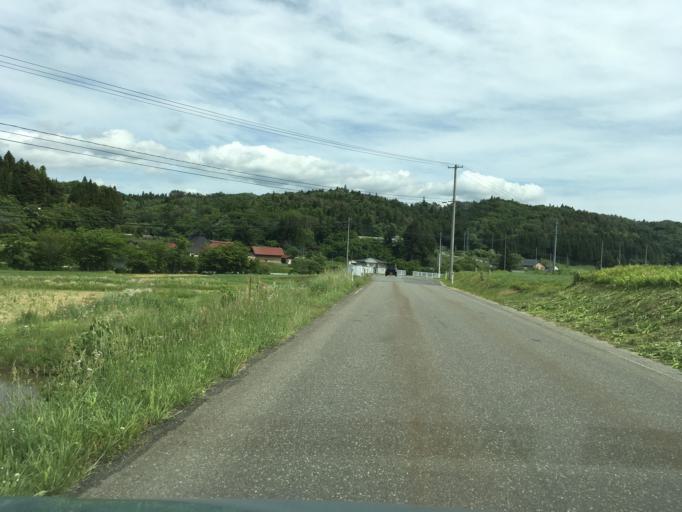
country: JP
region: Iwate
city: Mizusawa
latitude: 39.0834
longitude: 141.3525
